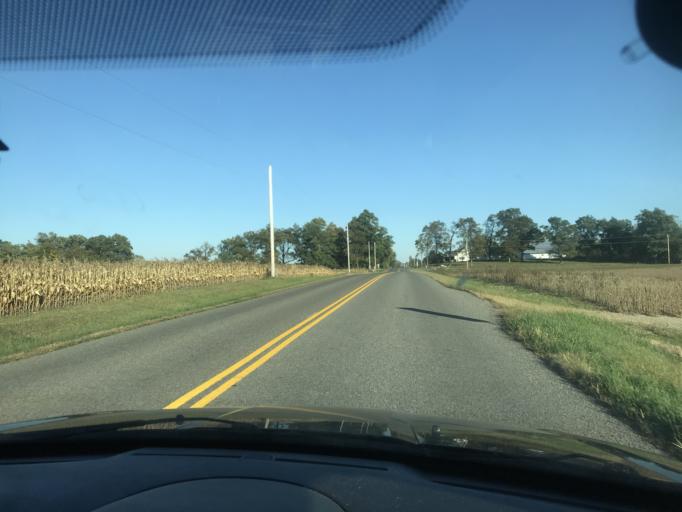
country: US
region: Ohio
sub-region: Logan County
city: De Graff
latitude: 40.3230
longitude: -83.8564
